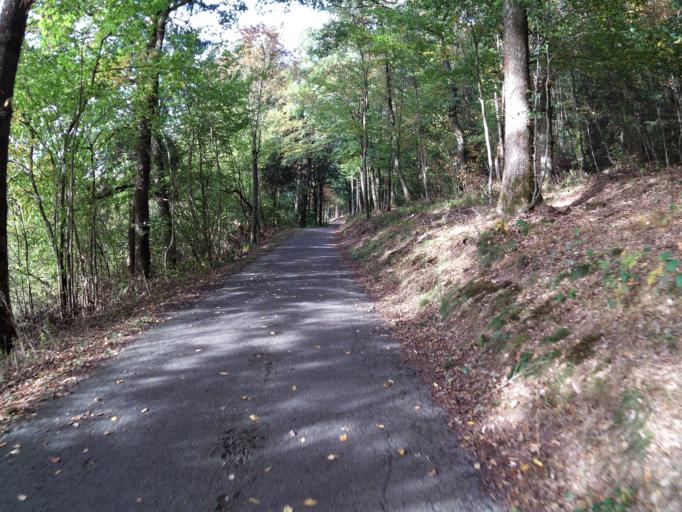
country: BE
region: Wallonia
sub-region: Province de Liege
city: Saint-Vith
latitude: 50.2708
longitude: 6.1376
